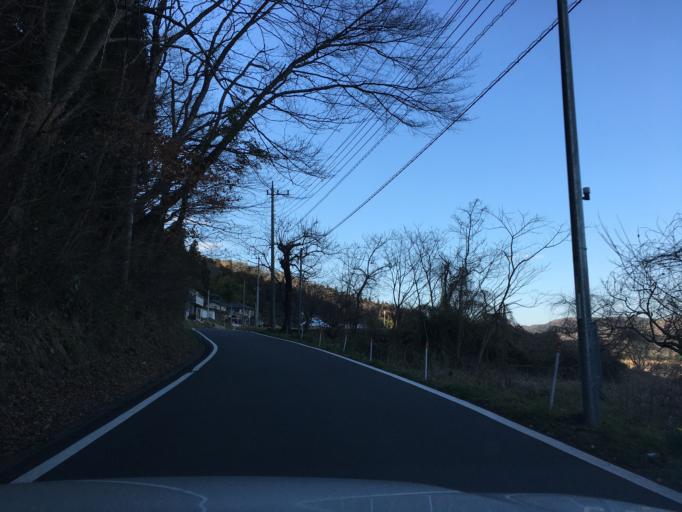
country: JP
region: Tochigi
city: Karasuyama
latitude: 36.7729
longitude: 140.2063
